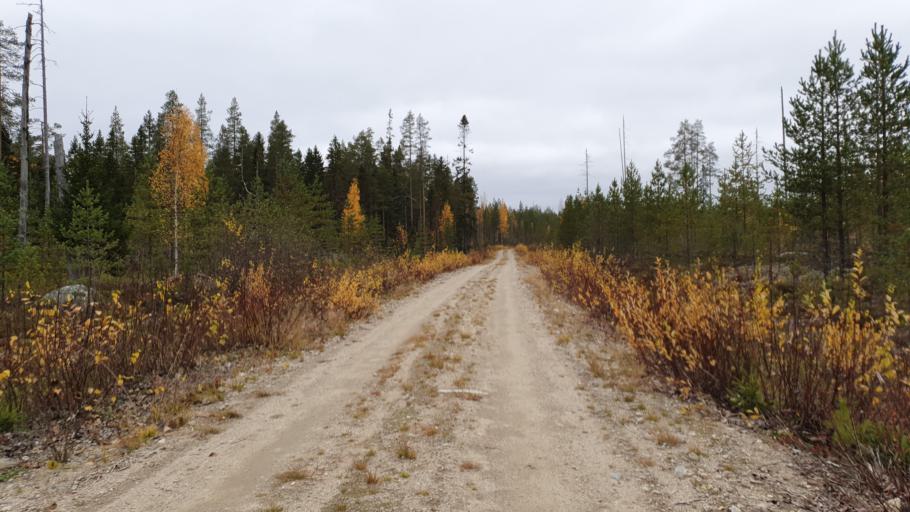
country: FI
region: Kainuu
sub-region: Kehys-Kainuu
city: Kuhmo
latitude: 64.4397
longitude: 29.6223
